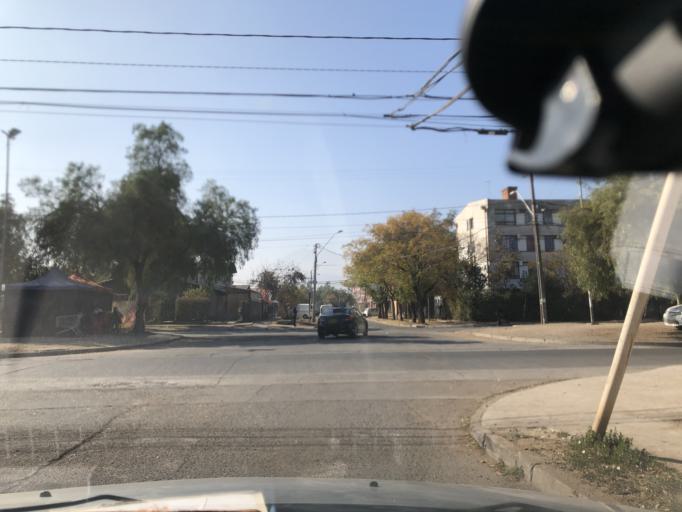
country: CL
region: Santiago Metropolitan
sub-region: Provincia de Cordillera
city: Puente Alto
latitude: -33.6303
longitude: -70.5899
